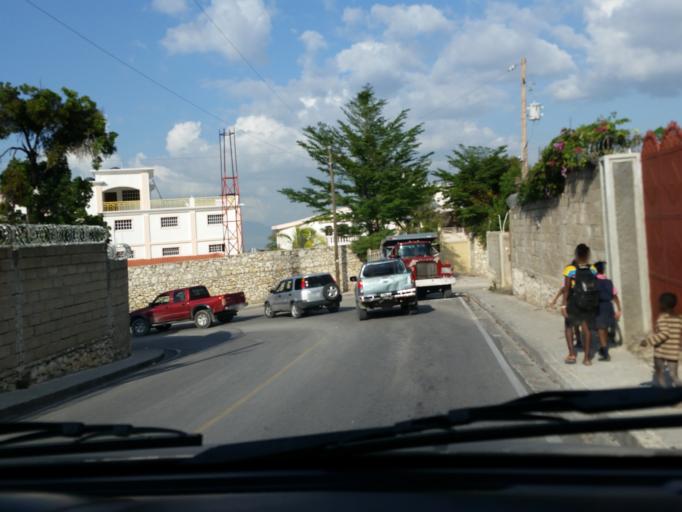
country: HT
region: Ouest
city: Petionville
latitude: 18.5187
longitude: -72.2739
